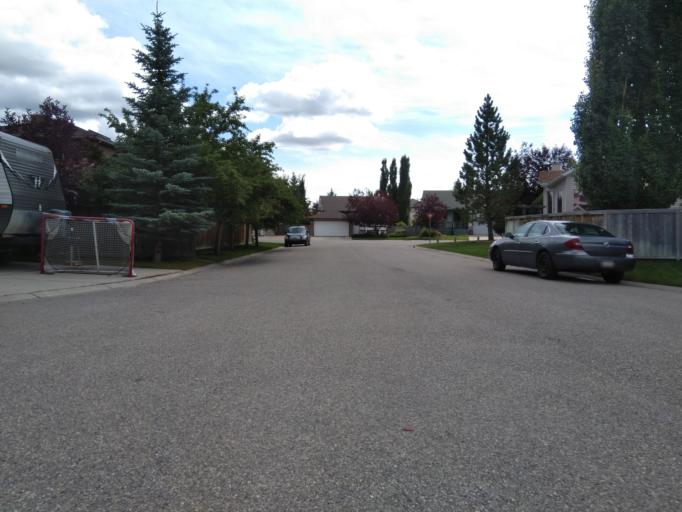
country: CA
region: Alberta
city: Cochrane
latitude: 51.1869
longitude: -114.4980
